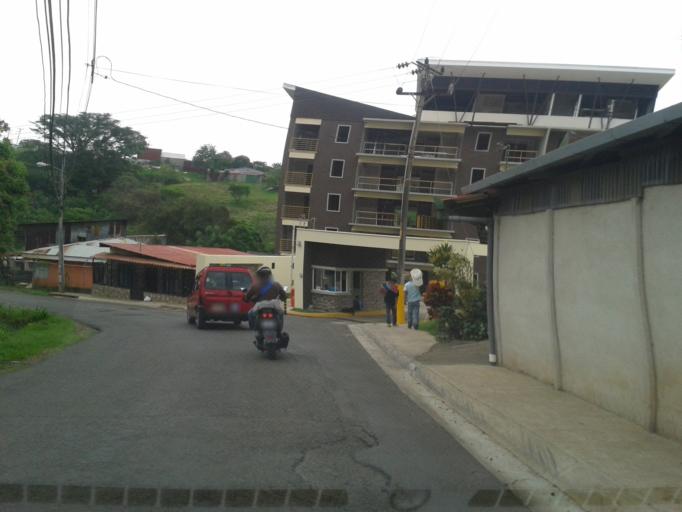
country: CR
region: Heredia
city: San Pablo
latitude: 9.9804
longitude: -84.1013
